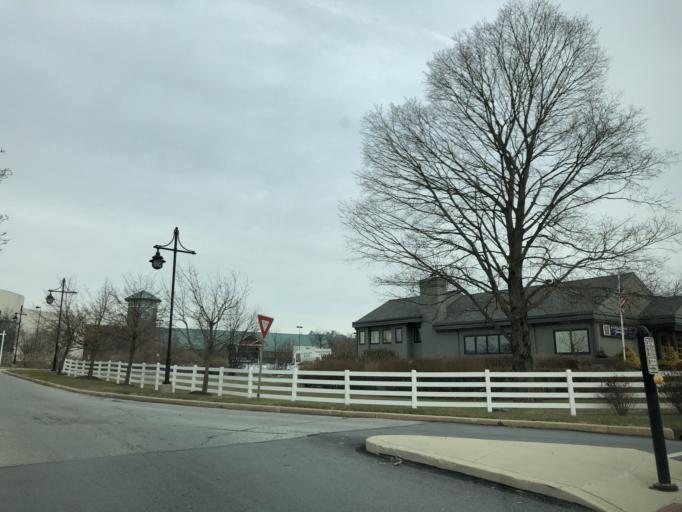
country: US
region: Pennsylvania
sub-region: Chester County
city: Exton
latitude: 40.0287
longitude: -75.6244
